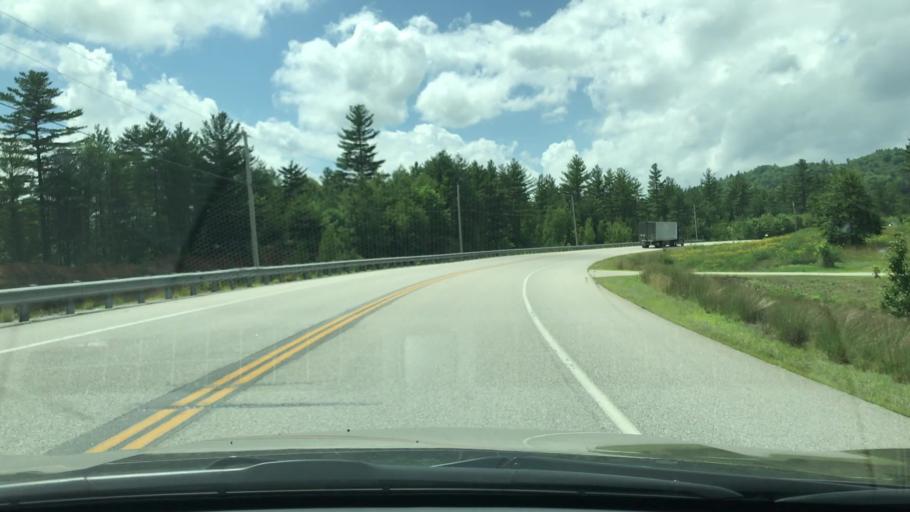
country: US
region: Maine
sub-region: Oxford County
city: Bethel
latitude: 44.3988
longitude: -70.8764
